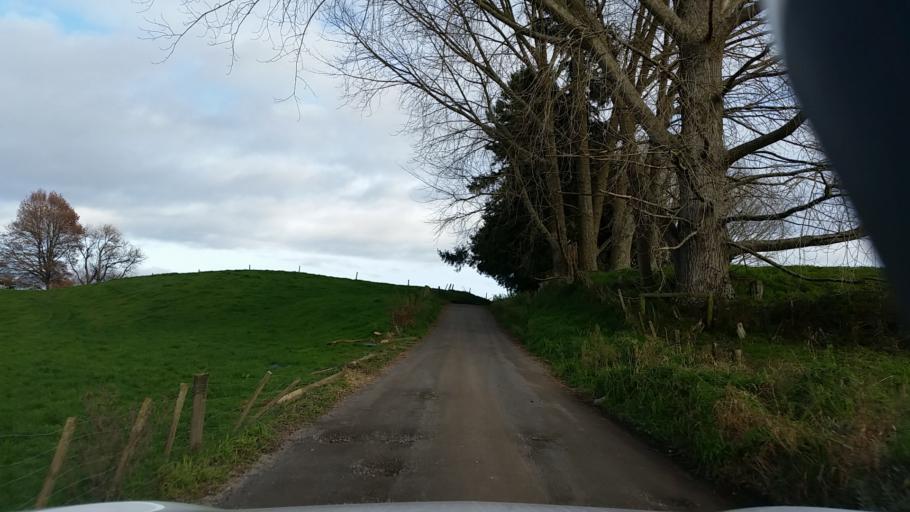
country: NZ
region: Bay of Plenty
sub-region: Rotorua District
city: Rotorua
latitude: -38.4532
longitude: 176.3413
